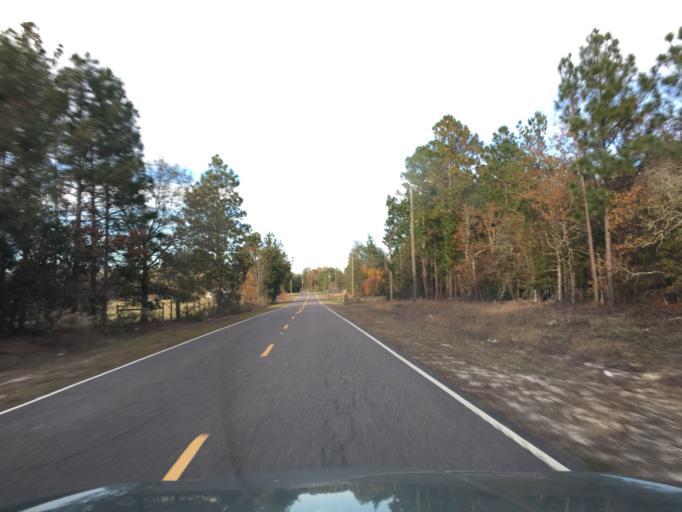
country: US
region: South Carolina
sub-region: Lexington County
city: Red Bank
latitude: 33.7013
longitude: -81.3580
